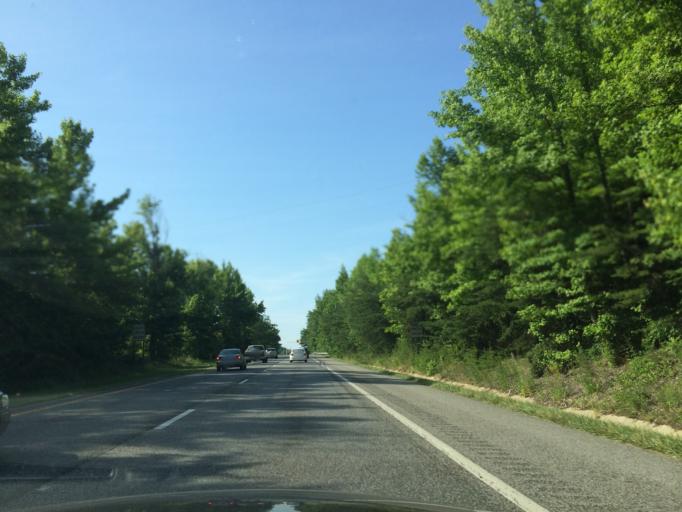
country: US
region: Maryland
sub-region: Prince George's County
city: Bowie
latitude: 38.9307
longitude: -76.7169
